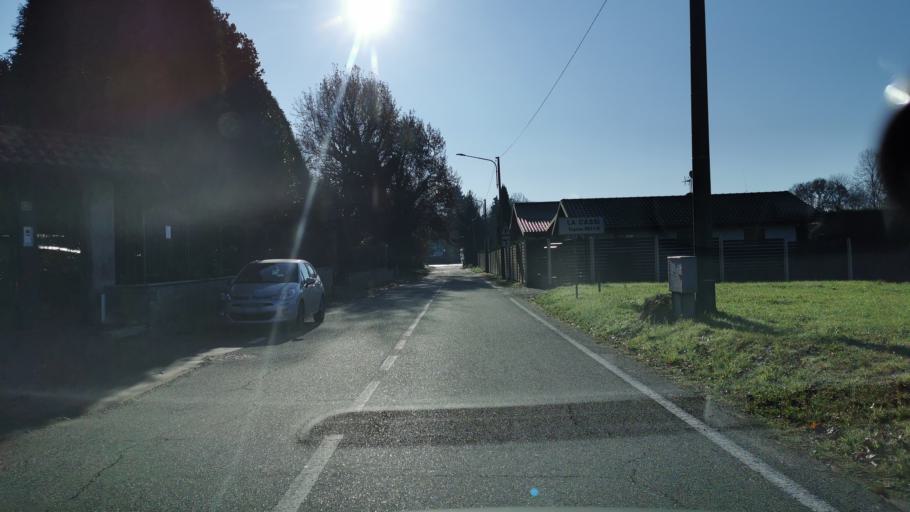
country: IT
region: Piedmont
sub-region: Provincia di Torino
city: Fiano
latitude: 45.2021
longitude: 7.5281
